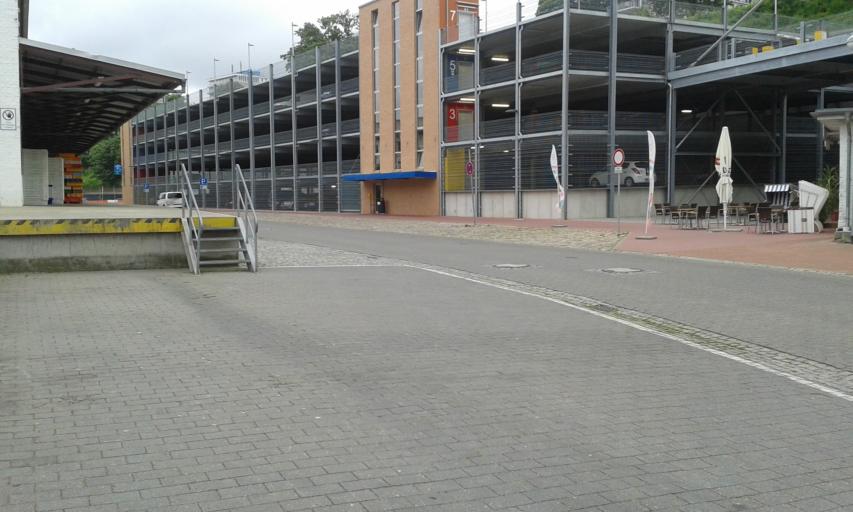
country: DE
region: Mecklenburg-Vorpommern
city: Sassnitz
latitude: 54.5147
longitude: 13.6491
